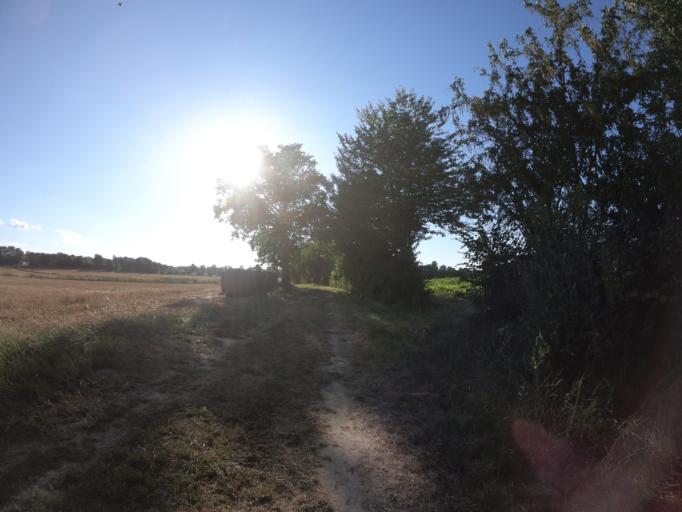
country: FR
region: Midi-Pyrenees
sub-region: Departement de l'Ariege
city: La Tour-du-Crieu
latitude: 43.0992
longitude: 1.7390
